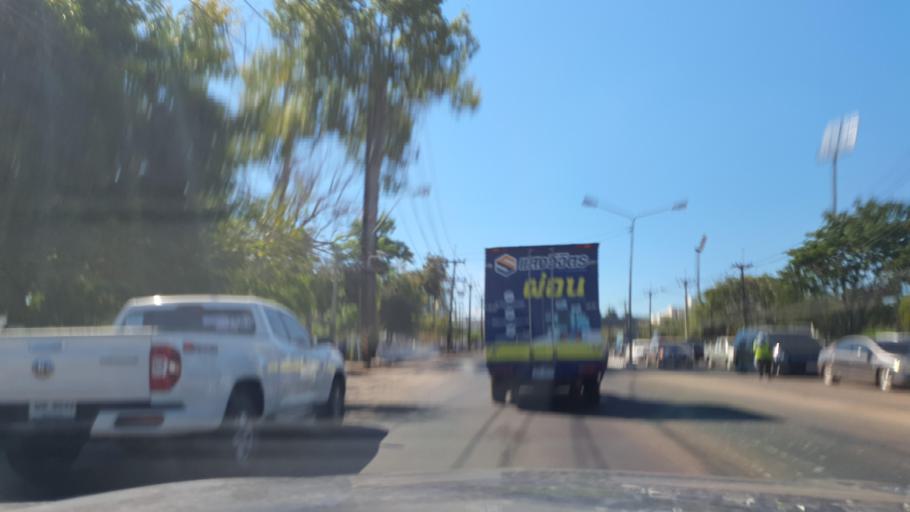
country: TH
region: Sakon Nakhon
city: Sakon Nakhon
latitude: 17.1913
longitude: 104.0952
